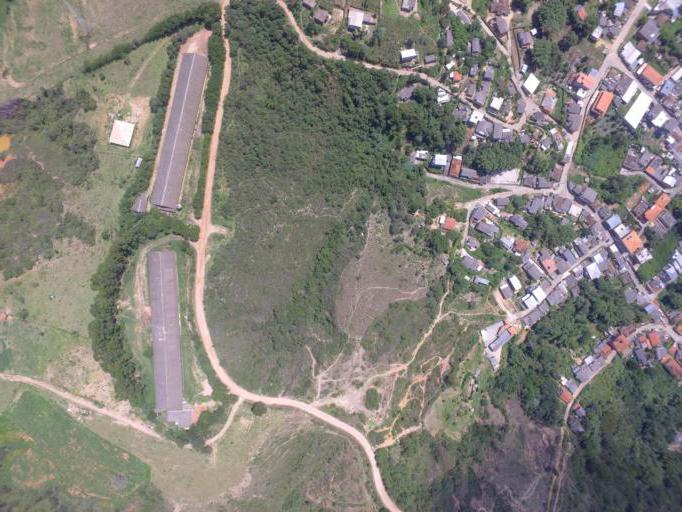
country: BR
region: Minas Gerais
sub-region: Tiradentes
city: Tiradentes
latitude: -21.0514
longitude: -44.0774
